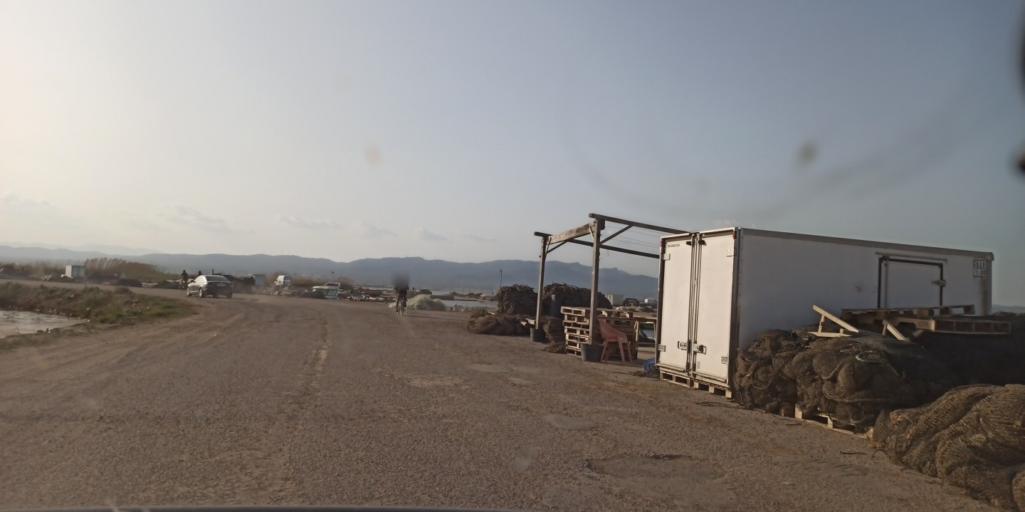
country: ES
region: Catalonia
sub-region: Provincia de Tarragona
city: L'Ampolla
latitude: 40.7664
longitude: 0.7395
